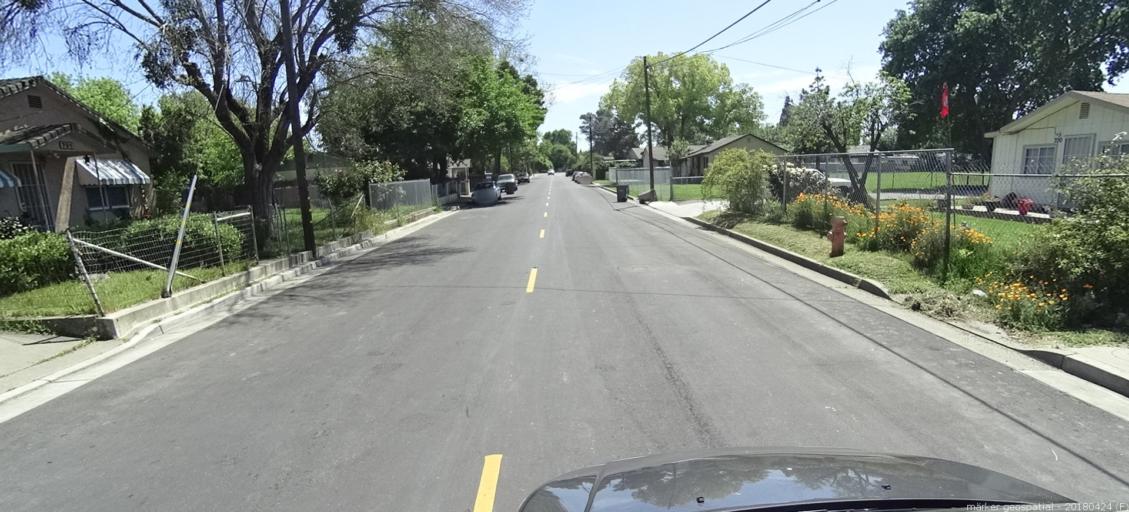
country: US
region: California
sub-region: Yolo County
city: West Sacramento
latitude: 38.5816
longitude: -121.5402
